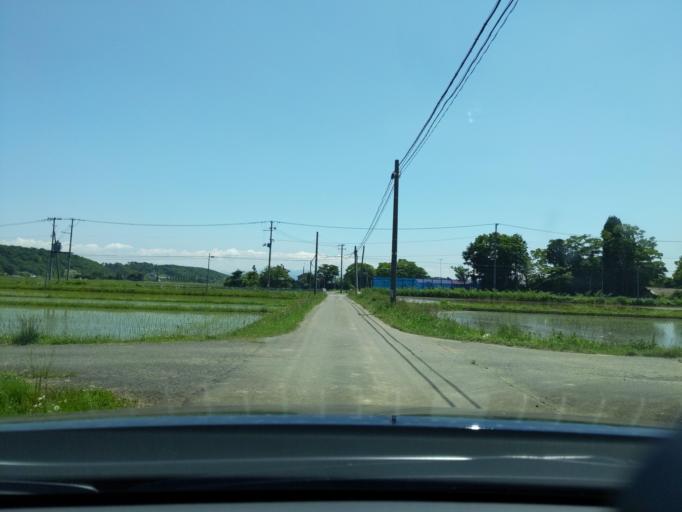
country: JP
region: Fukushima
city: Koriyama
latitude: 37.3948
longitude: 140.2869
